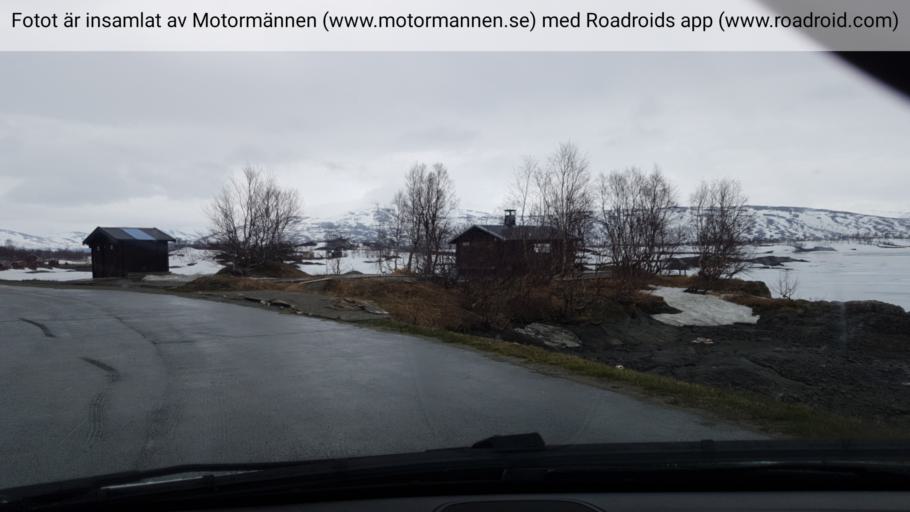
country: NO
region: Nordland
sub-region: Rana
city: Mo i Rana
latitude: 66.1354
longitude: 14.5910
